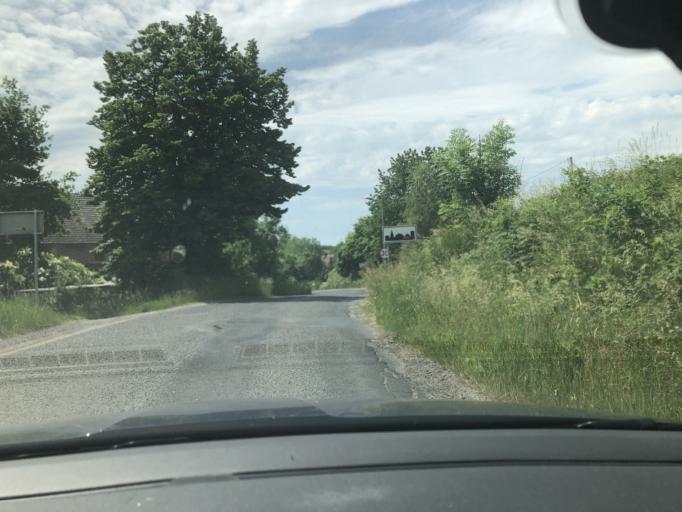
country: PL
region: Lower Silesian Voivodeship
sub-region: Powiat zlotoryjski
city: Wilkow
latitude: 51.0991
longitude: 15.9170
